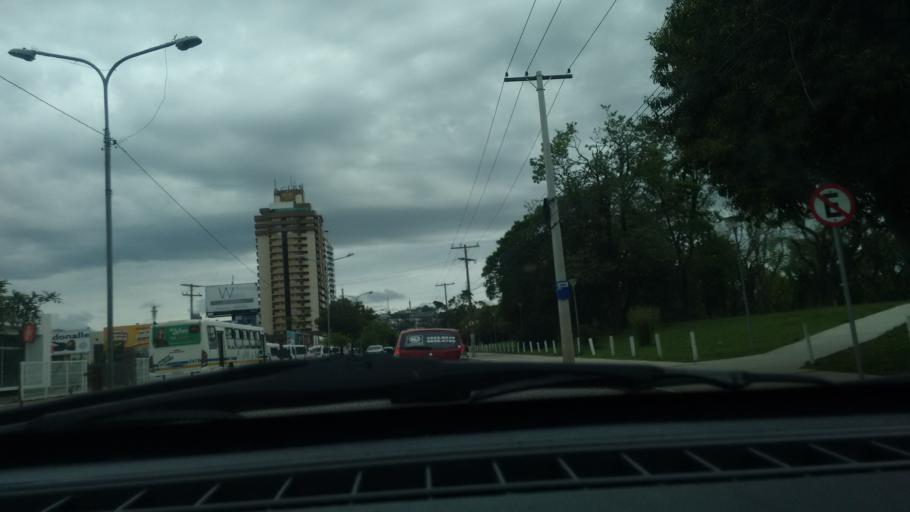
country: BR
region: Rio Grande do Sul
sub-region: Porto Alegre
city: Porto Alegre
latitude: -30.0524
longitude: -51.2300
